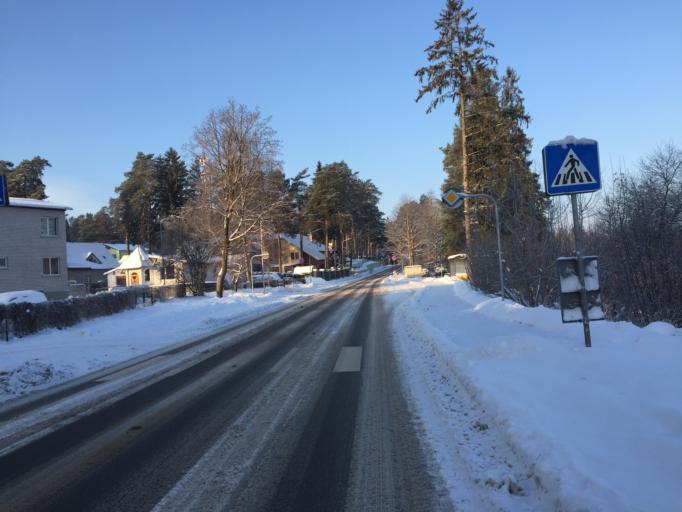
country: LV
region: Ogre
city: Ogre
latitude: 56.8065
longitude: 24.6281
